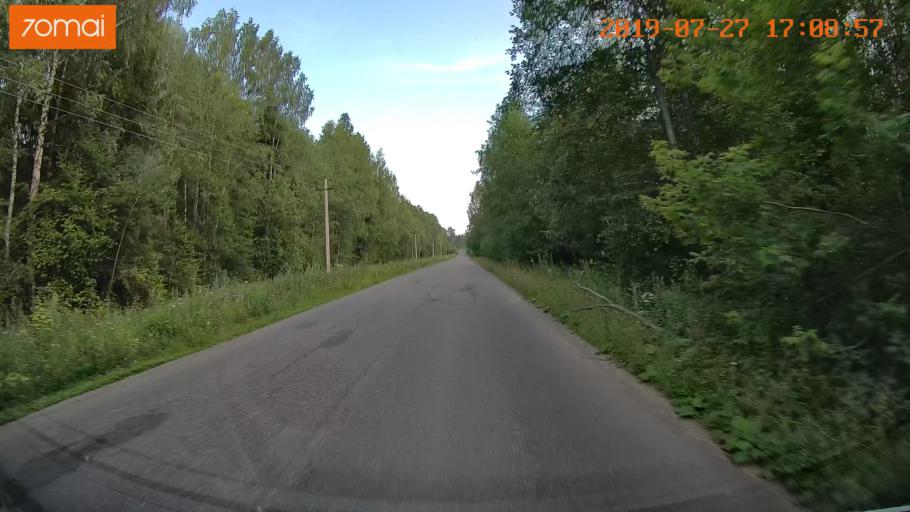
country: RU
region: Ivanovo
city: Novo-Talitsy
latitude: 57.0782
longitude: 40.8436
